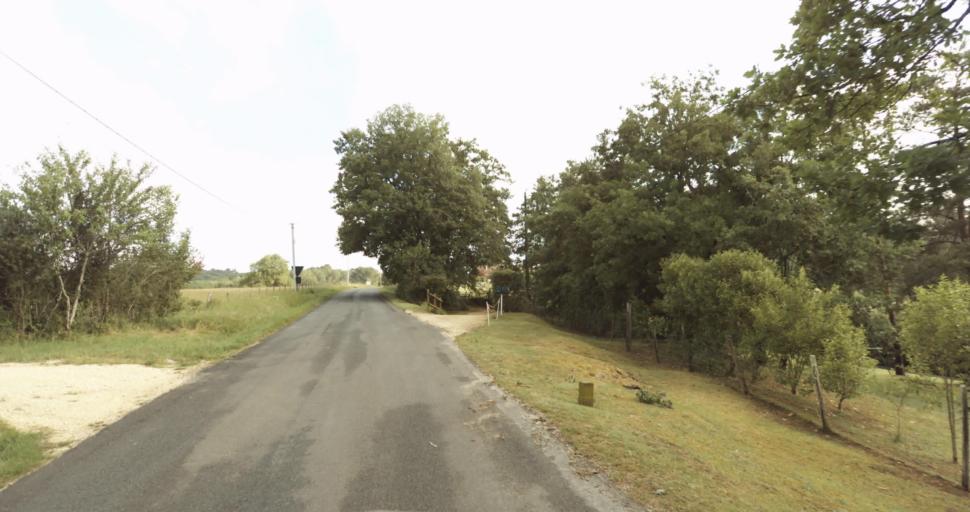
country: FR
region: Aquitaine
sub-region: Departement de la Dordogne
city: Le Bugue
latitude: 44.9238
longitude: 0.8225
